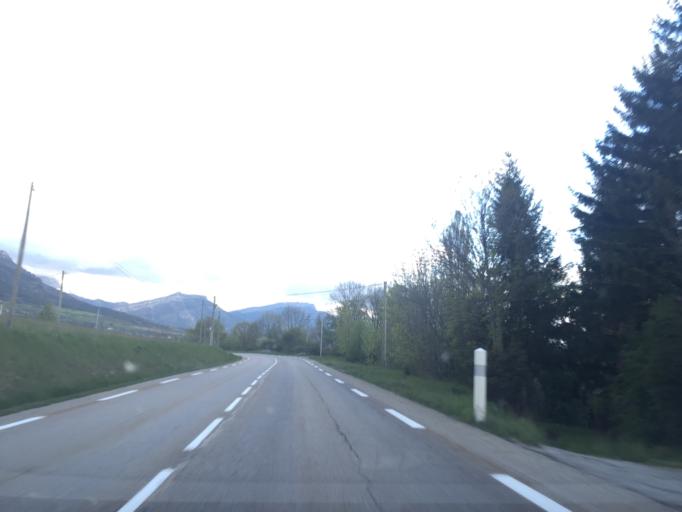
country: FR
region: Rhone-Alpes
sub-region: Departement de l'Isere
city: Mens
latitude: 44.7790
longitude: 5.6528
